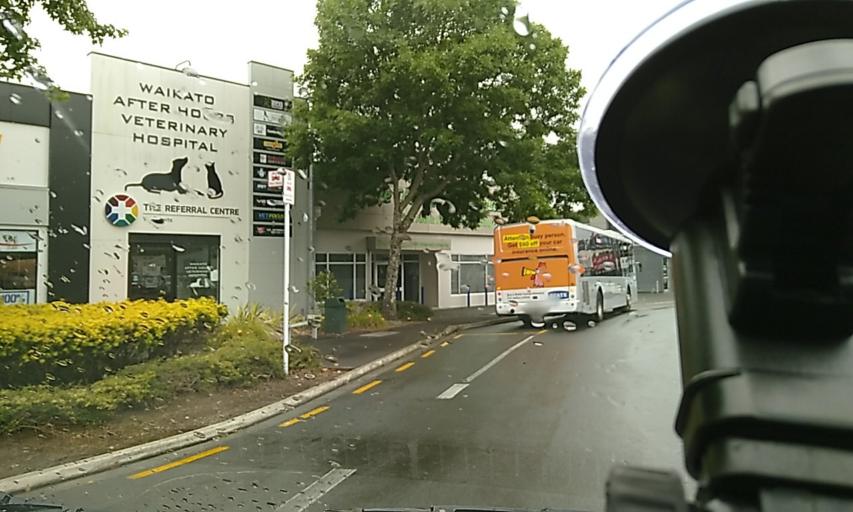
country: NZ
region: Waikato
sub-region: Hamilton City
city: Hamilton
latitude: -37.7812
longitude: 175.2739
